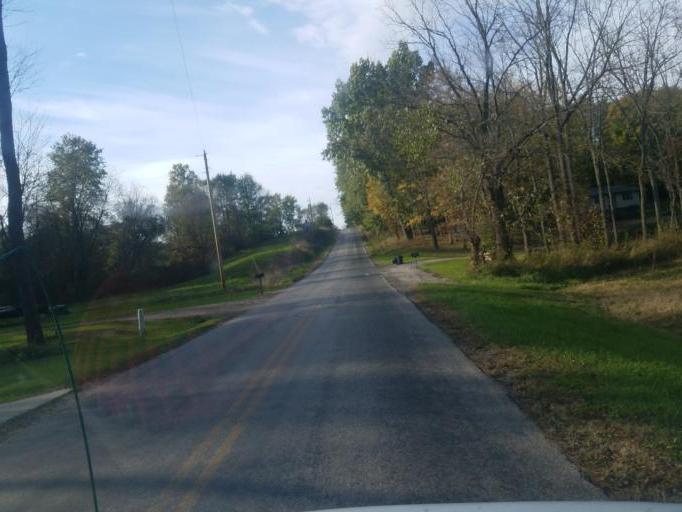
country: US
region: Ohio
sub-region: Wayne County
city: Shreve
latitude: 40.6570
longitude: -82.0719
